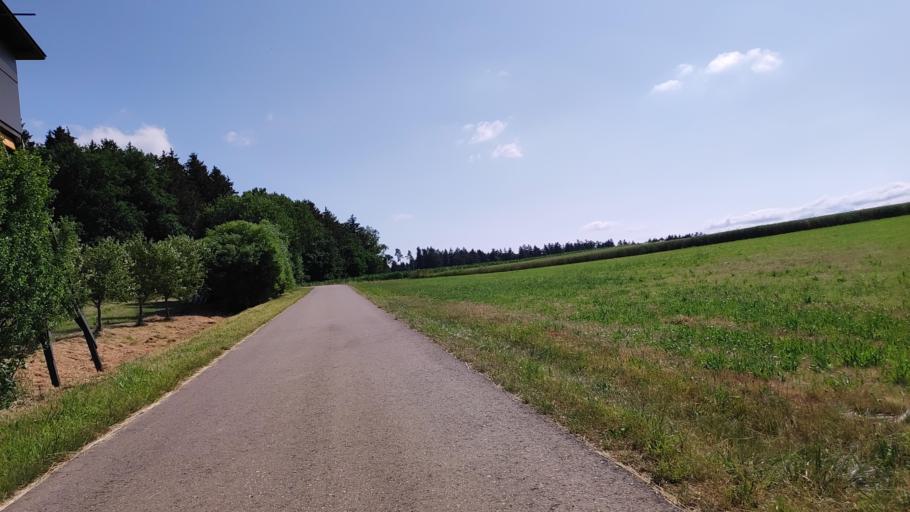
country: DE
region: Bavaria
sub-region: Swabia
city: Holzheim
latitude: 48.4954
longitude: 10.5551
